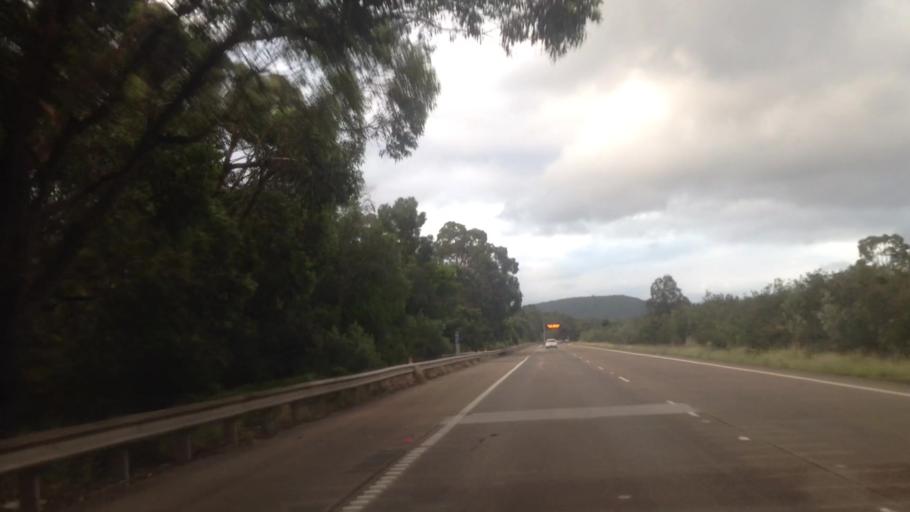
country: AU
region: New South Wales
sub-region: Wyong Shire
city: Charmhaven
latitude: -33.1798
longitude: 151.4672
